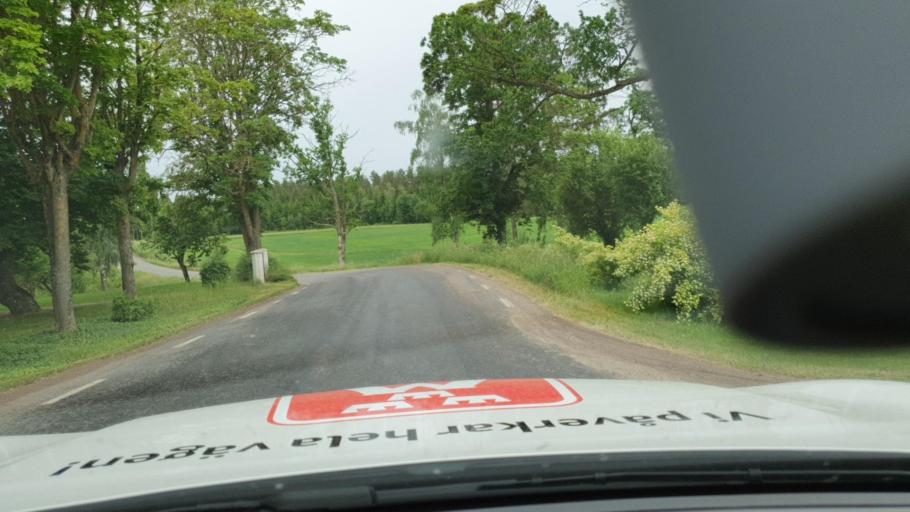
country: SE
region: Vaestra Goetaland
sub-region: Tidaholms Kommun
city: Olofstorp
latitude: 58.3139
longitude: 14.0619
